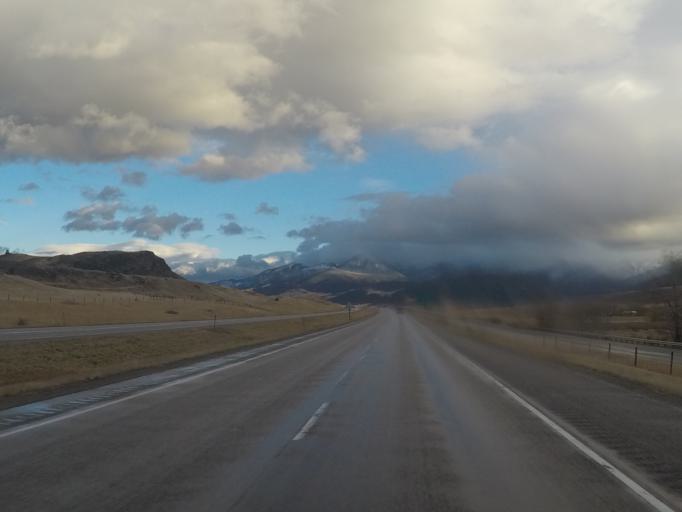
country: US
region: Montana
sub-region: Park County
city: Livingston
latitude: 45.6600
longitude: -110.6366
